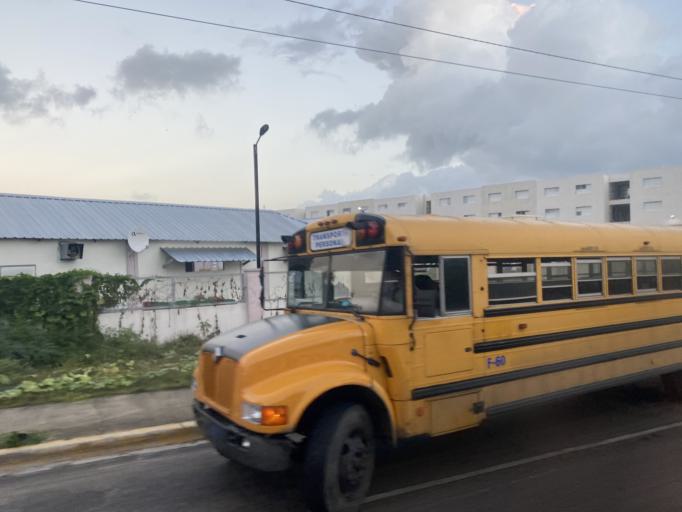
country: DO
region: San Juan
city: Punta Cana
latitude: 18.7061
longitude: -68.4658
